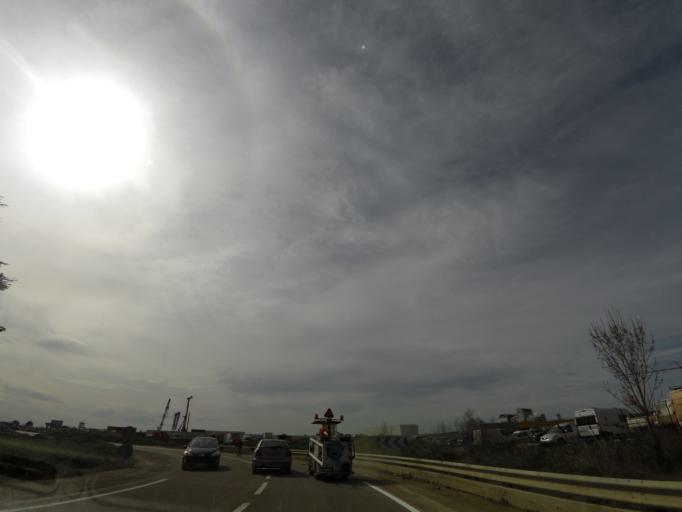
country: FR
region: Languedoc-Roussillon
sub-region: Departement du Gard
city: Gallargues-le-Montueux
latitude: 43.7063
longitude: 4.1904
